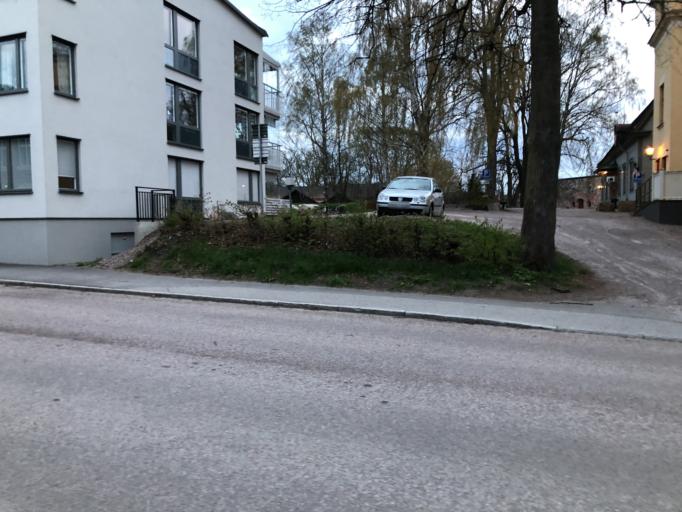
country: SE
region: Soedermanland
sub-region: Nykopings Kommun
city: Nykoping
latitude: 58.7486
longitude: 17.0085
